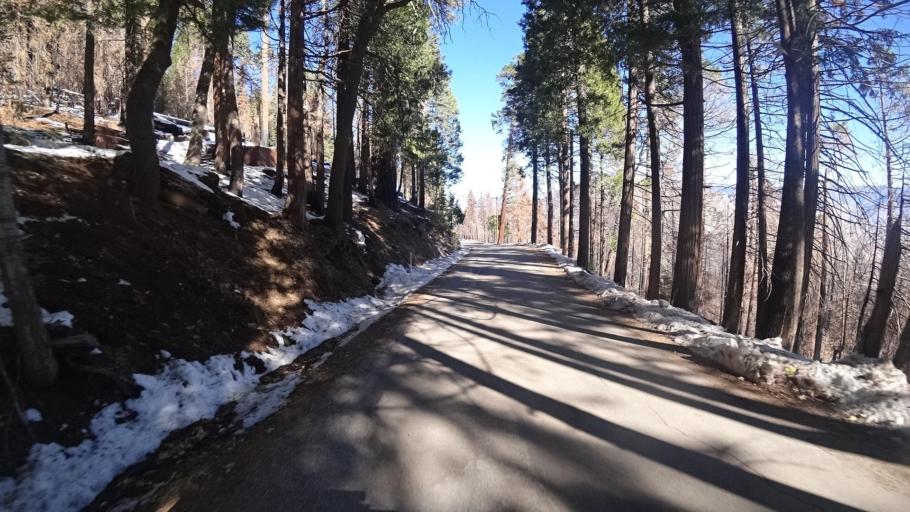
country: US
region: California
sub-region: Kern County
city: Alta Sierra
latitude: 35.7159
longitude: -118.5549
